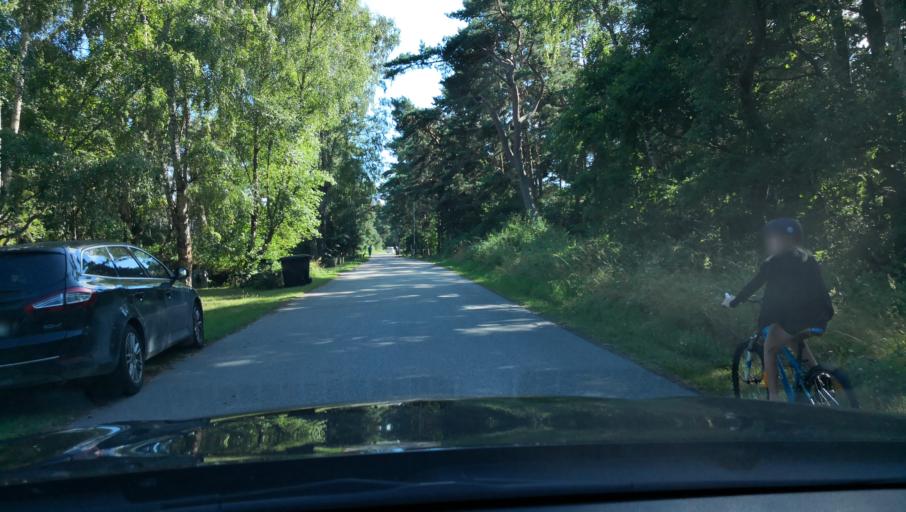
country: SE
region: Skane
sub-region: Simrishamns Kommun
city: Kivik
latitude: 55.7842
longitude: 14.1953
